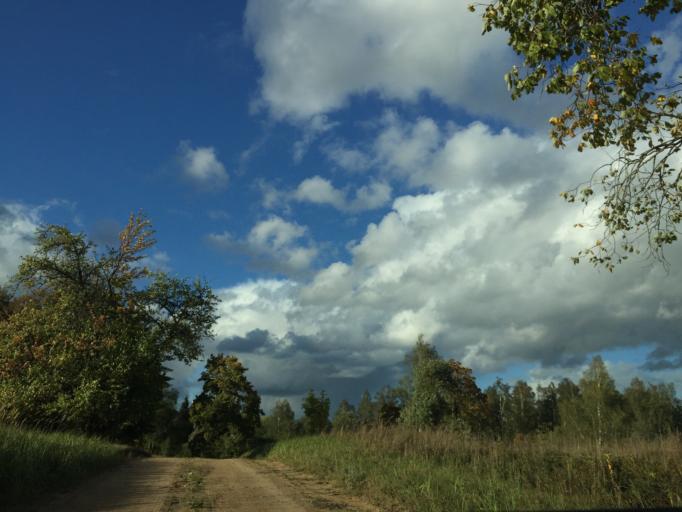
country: LV
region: Ligatne
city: Ligatne
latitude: 57.1294
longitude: 25.1258
